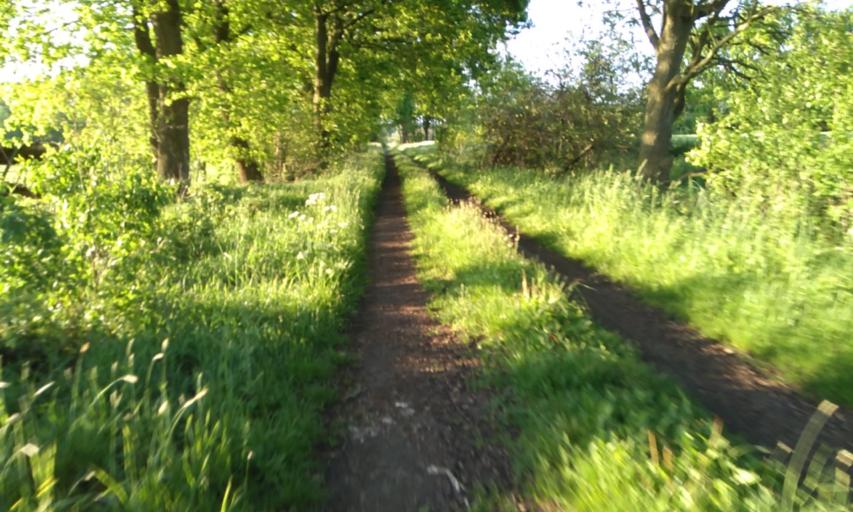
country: DE
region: Lower Saxony
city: Bliedersdorf
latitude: 53.4923
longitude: 9.5664
